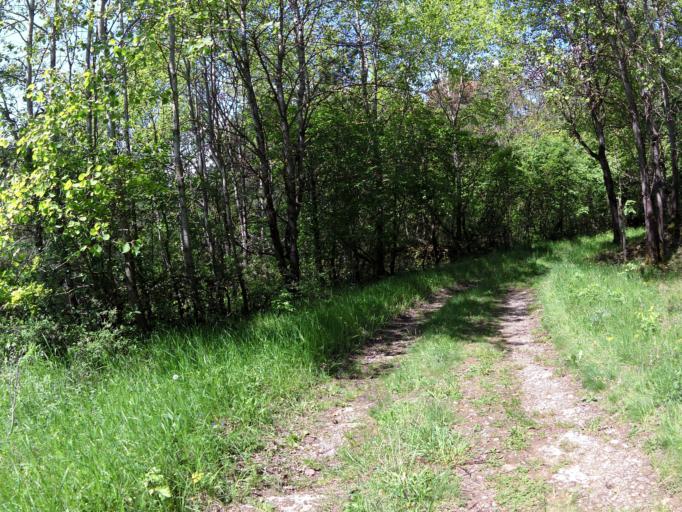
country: DE
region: Bavaria
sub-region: Regierungsbezirk Unterfranken
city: Theilheim
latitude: 49.7385
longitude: 10.0155
